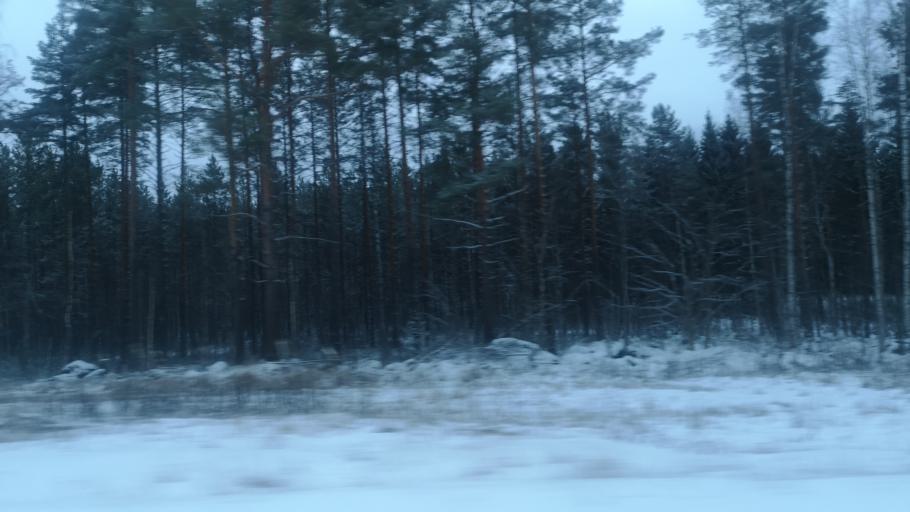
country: FI
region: Southern Savonia
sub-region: Savonlinna
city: Enonkoski
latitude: 62.1017
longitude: 28.6508
